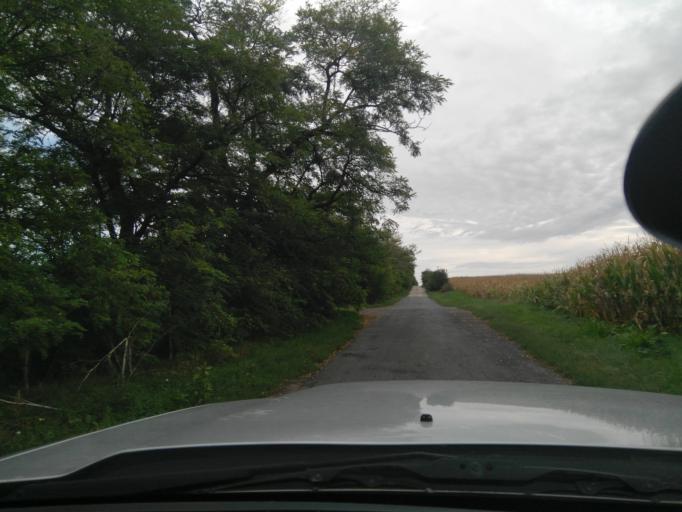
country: HU
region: Fejer
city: Martonvasar
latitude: 47.3551
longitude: 18.7780
